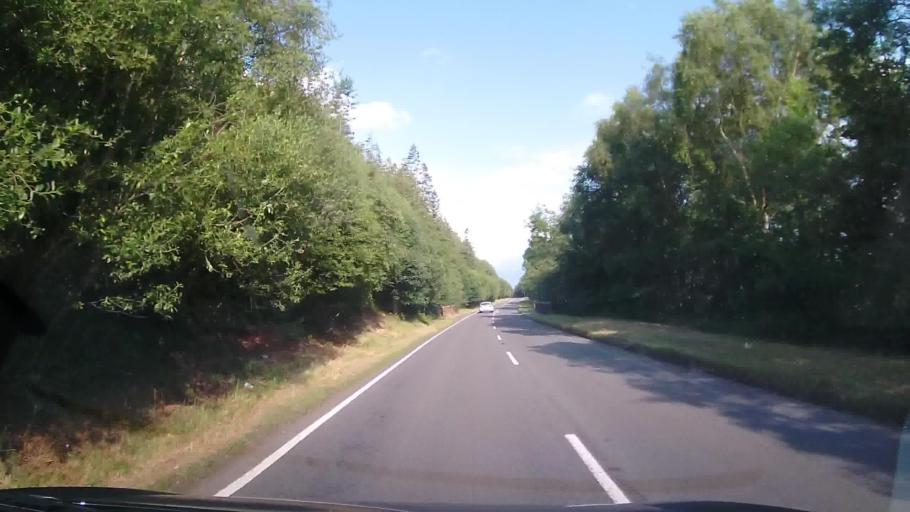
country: GB
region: Wales
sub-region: Gwynedd
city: Bala
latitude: 52.9506
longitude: -3.6770
